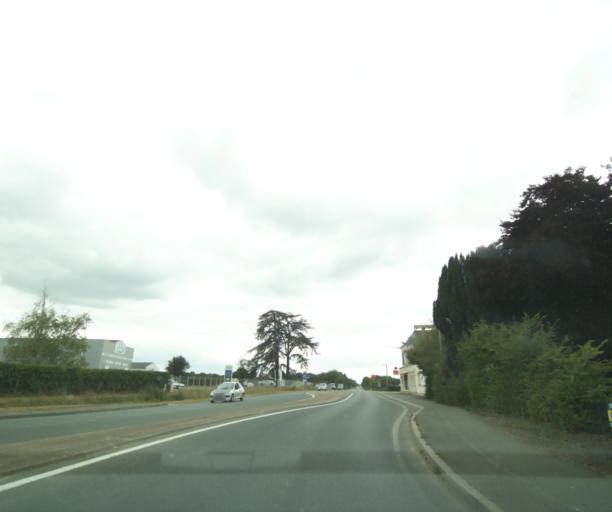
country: FR
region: Pays de la Loire
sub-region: Departement de Maine-et-Loire
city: Pellouailles-les-Vignes
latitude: 47.5156
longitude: -0.4580
